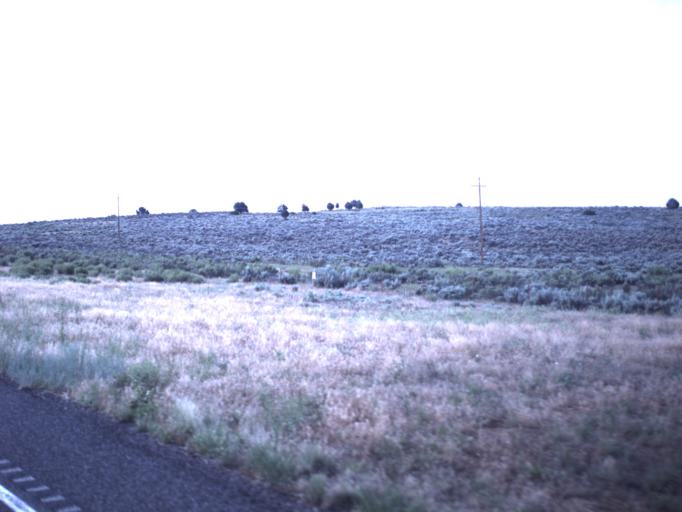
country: US
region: Utah
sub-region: Kane County
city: Kanab
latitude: 37.2302
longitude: -112.7305
